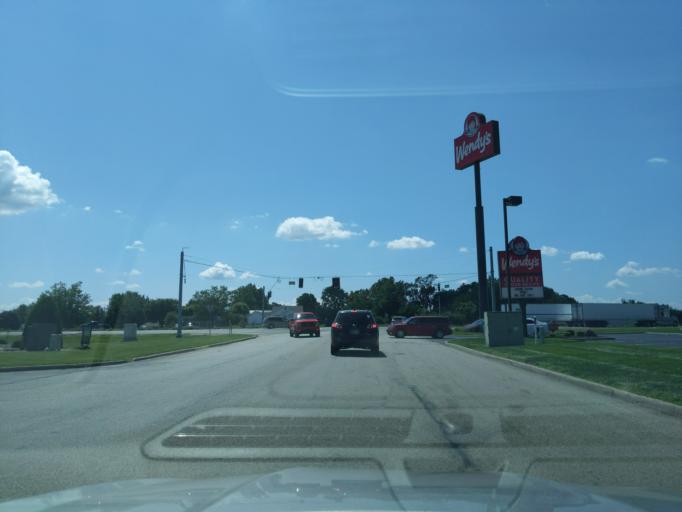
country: US
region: Indiana
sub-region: Decatur County
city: Greensburg
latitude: 39.3549
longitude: -85.4844
